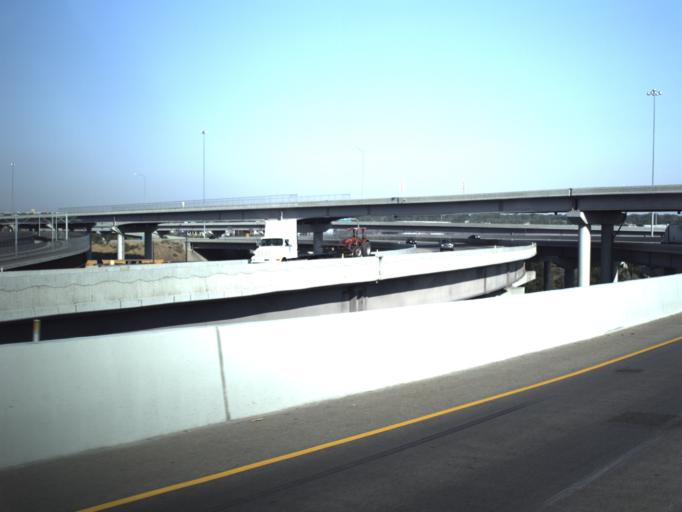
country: US
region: Utah
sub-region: Salt Lake County
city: South Salt Lake
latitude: 40.7230
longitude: -111.9058
